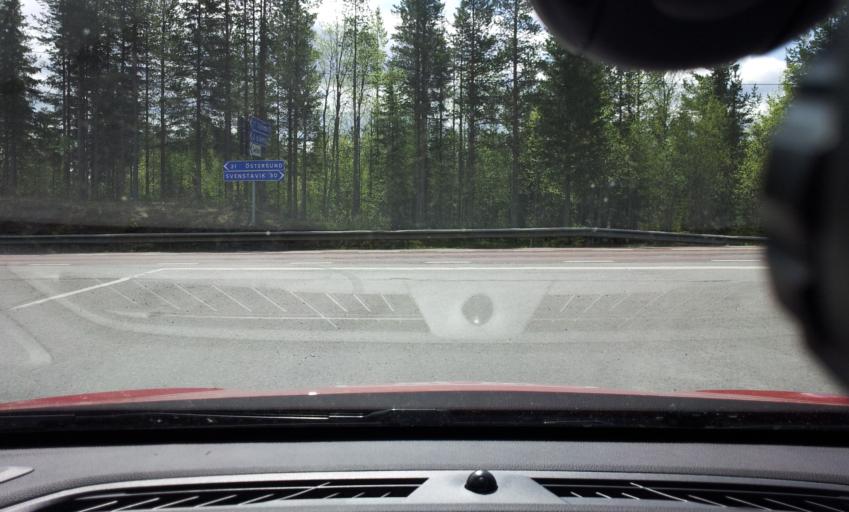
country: SE
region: Jaemtland
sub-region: OEstersunds Kommun
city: Ostersund
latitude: 63.0016
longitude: 14.6424
